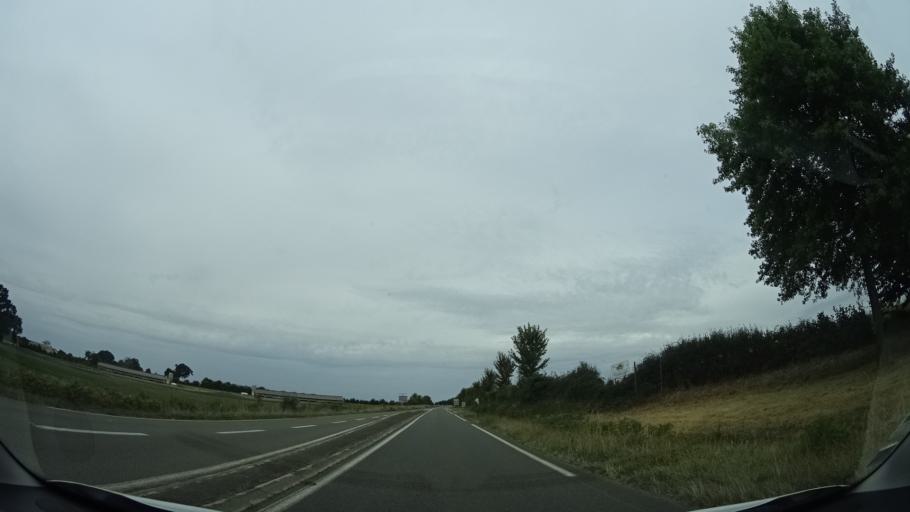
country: FR
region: Pays de la Loire
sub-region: Departement de la Mayenne
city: Meslay-du-Maine
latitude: 47.9434
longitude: -0.5207
